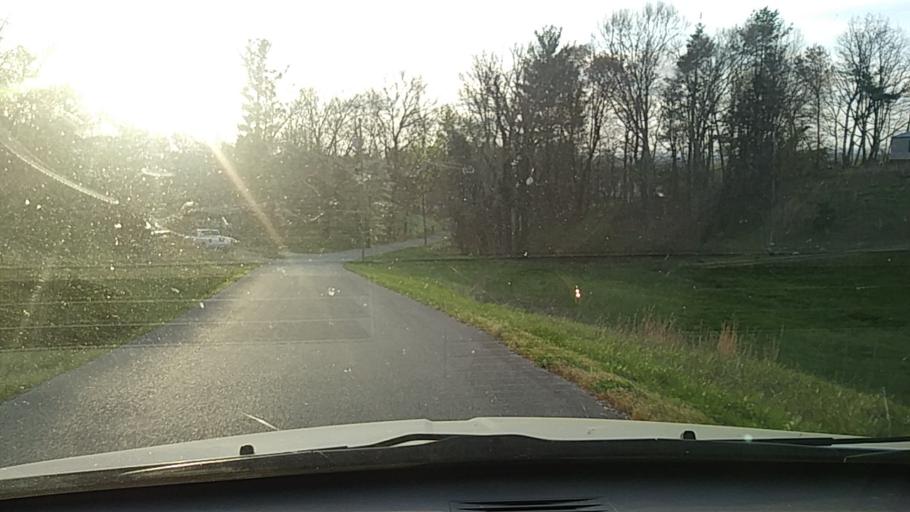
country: US
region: Tennessee
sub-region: Greene County
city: Tusculum
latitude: 36.0945
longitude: -82.7043
